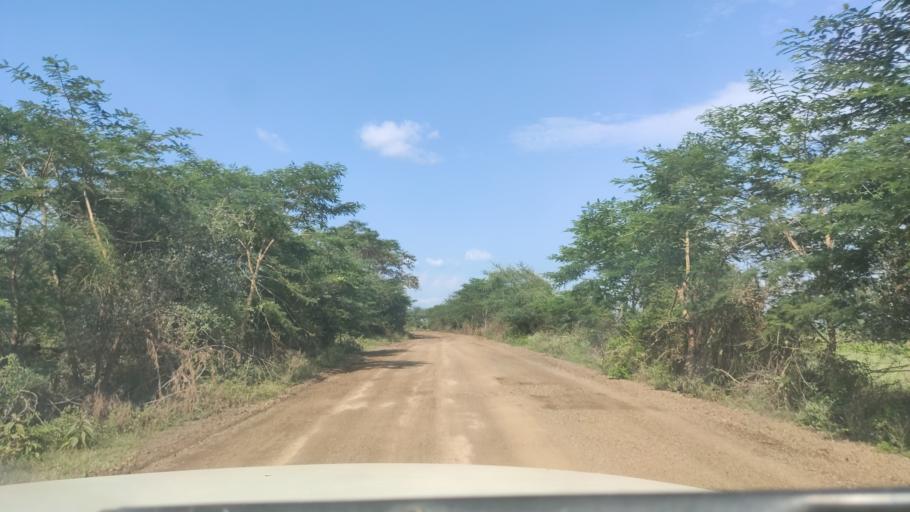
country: ET
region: Southern Nations, Nationalities, and People's Region
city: Felege Neway
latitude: 6.3820
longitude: 37.0930
